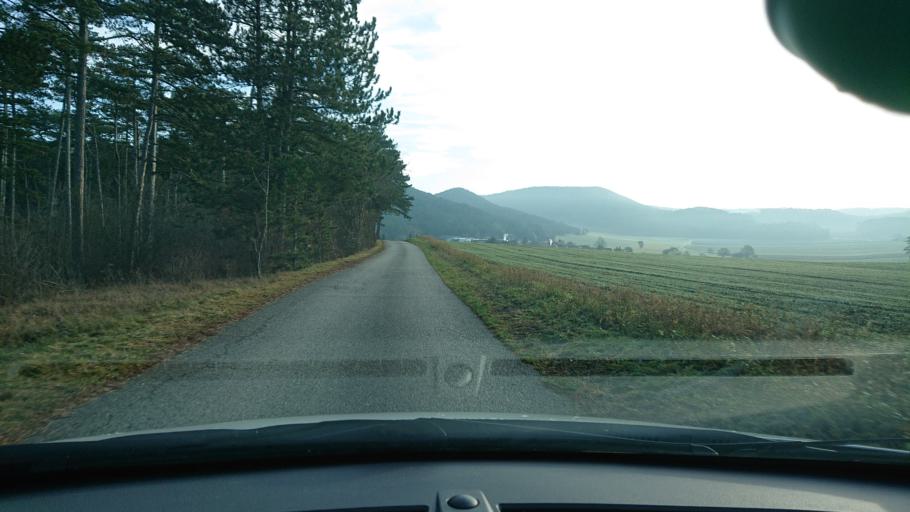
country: AT
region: Lower Austria
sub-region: Politischer Bezirk Baden
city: Berndorf
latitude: 47.9296
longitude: 16.1058
